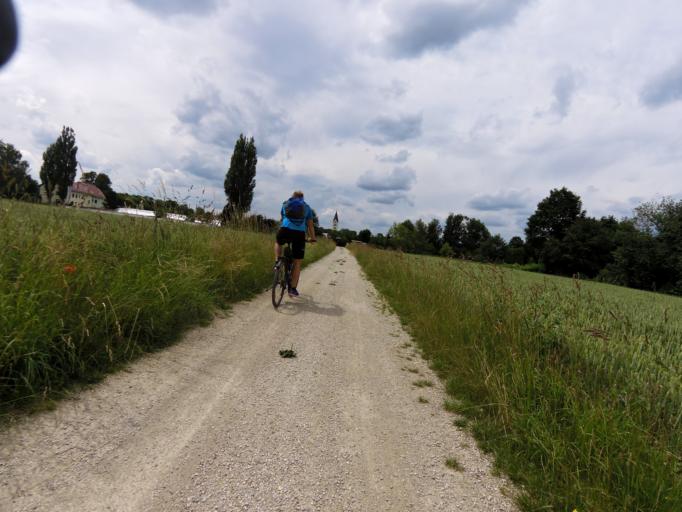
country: DE
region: Bavaria
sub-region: Upper Bavaria
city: Allershausen
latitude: 48.4324
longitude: 11.6102
